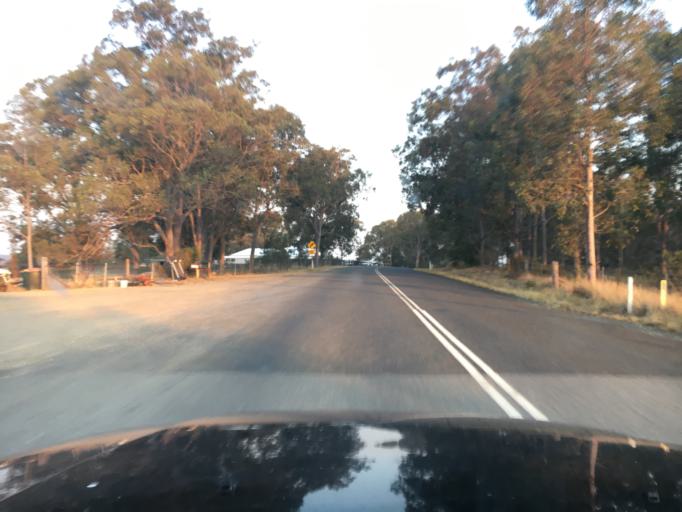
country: AU
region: New South Wales
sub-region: Cessnock
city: Branxton
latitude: -32.6167
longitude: 151.3557
